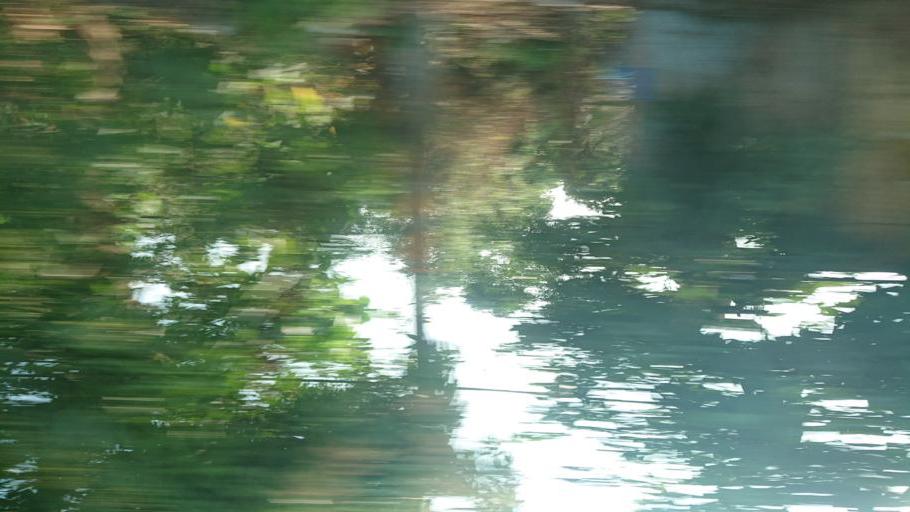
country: TW
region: Taiwan
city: Xinying
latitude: 23.1572
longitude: 120.2498
